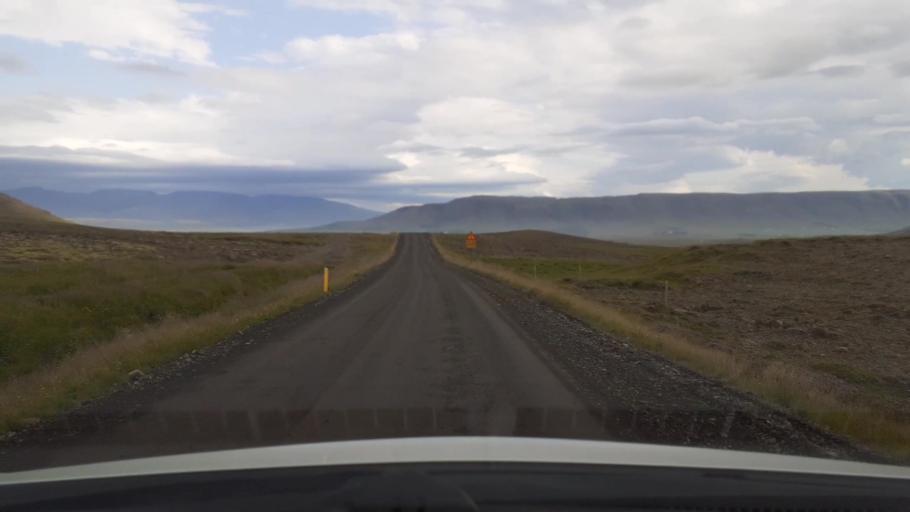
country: IS
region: Capital Region
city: Mosfellsbaer
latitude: 64.3035
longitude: -21.6582
